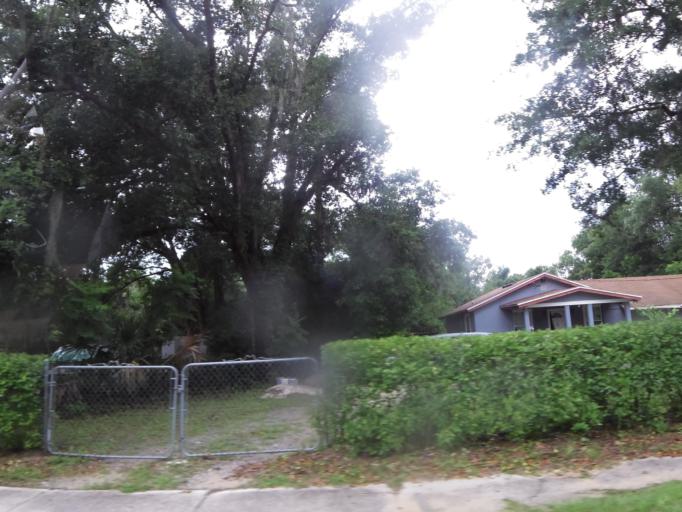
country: US
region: Florida
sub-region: Duval County
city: Jacksonville
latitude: 30.3048
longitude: -81.5477
